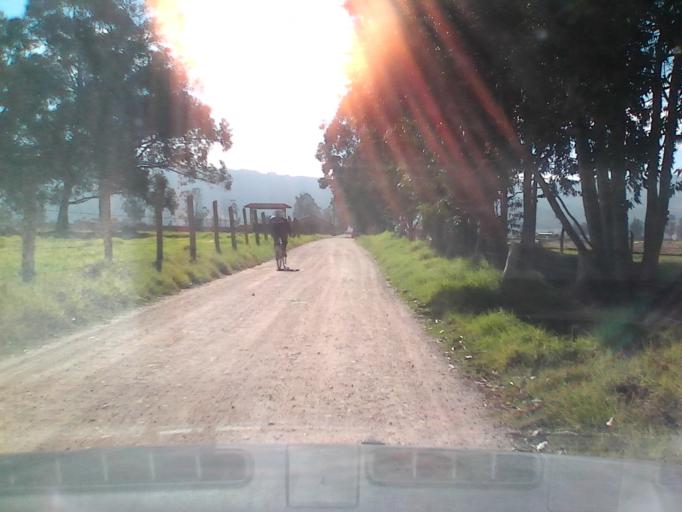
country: CO
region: Boyaca
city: Duitama
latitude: 5.7828
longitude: -73.0415
